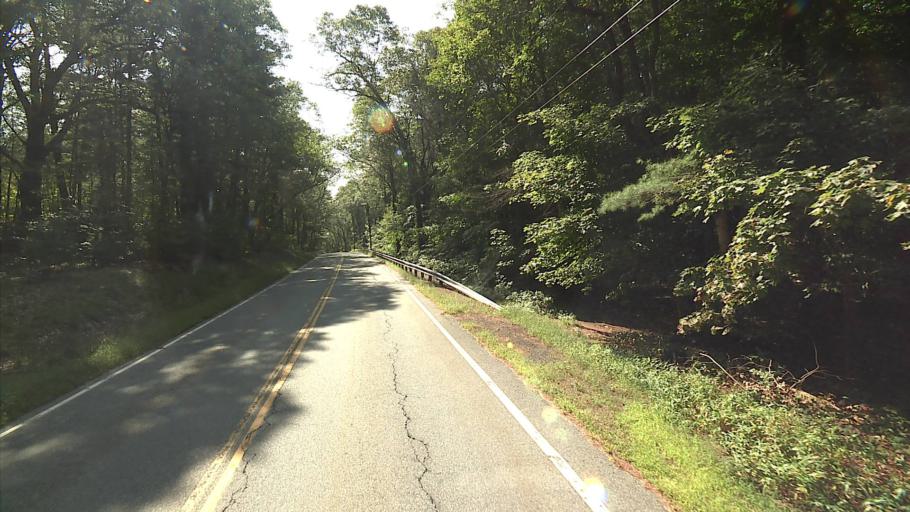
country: US
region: Massachusetts
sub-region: Worcester County
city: Southbridge
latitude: 42.0223
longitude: -72.0093
